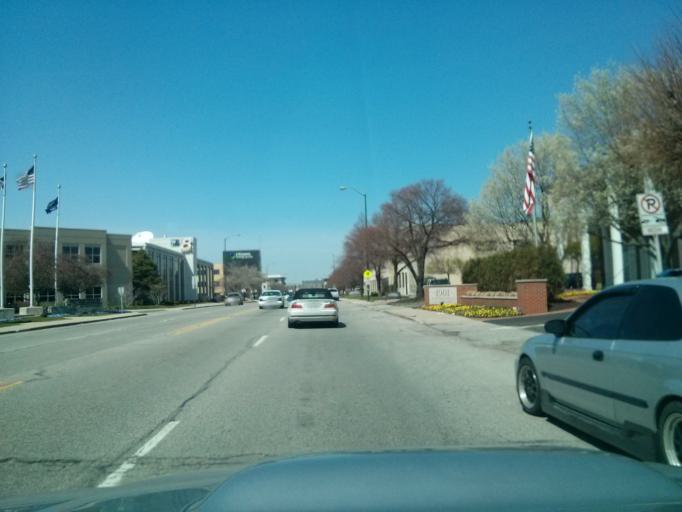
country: US
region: Indiana
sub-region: Marion County
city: Indianapolis
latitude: 39.7919
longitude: -86.1573
